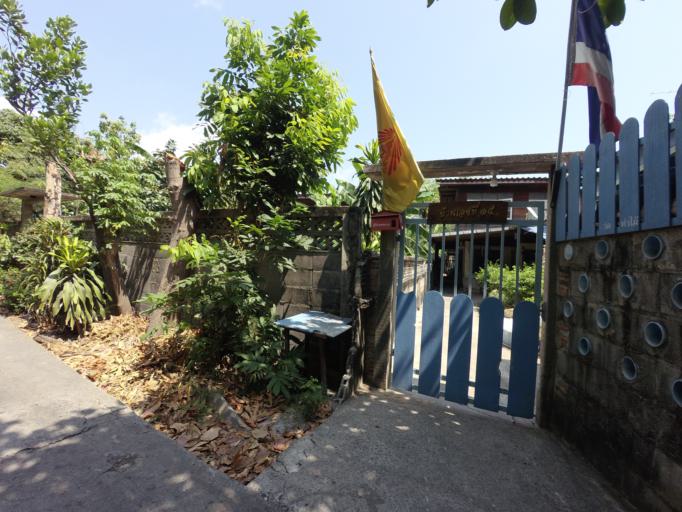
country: TH
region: Bangkok
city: Rat Burana
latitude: 13.6607
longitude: 100.5070
